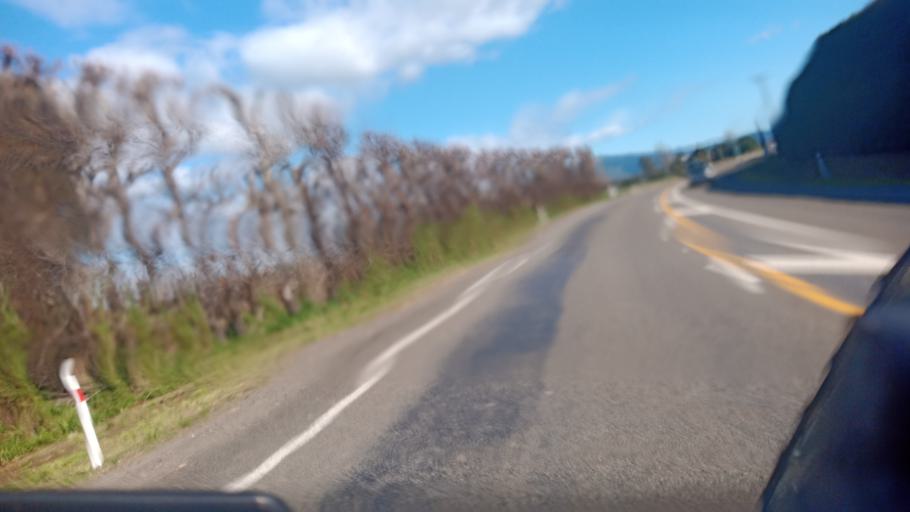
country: NZ
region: Bay of Plenty
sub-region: Opotiki District
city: Opotiki
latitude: -38.0011
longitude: 177.2973
